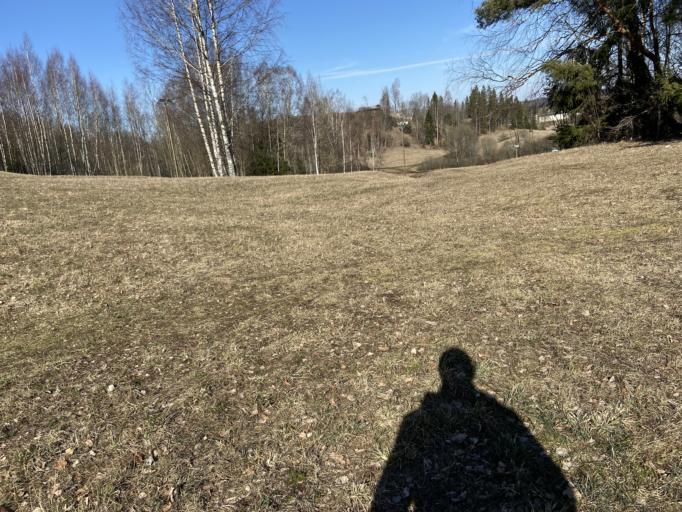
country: EE
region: Tartu
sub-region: Elva linn
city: Elva
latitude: 58.0545
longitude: 26.5077
